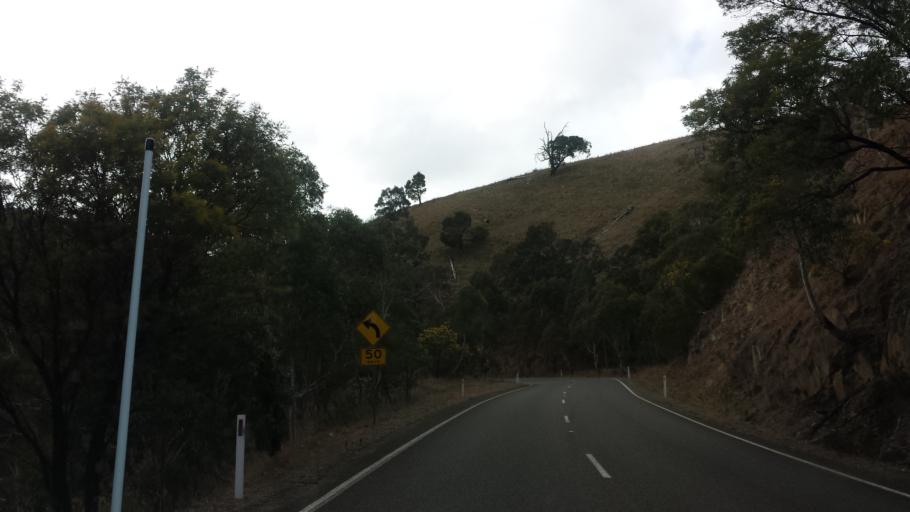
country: AU
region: Victoria
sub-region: Alpine
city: Mount Beauty
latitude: -37.1145
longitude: 147.5620
